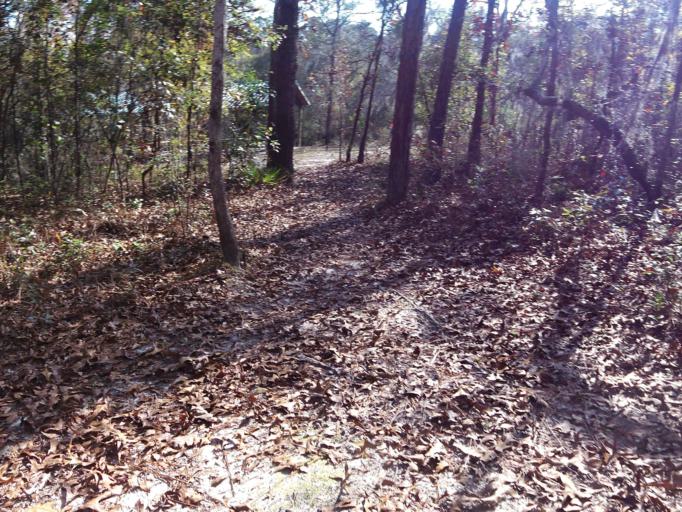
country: US
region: Florida
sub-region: Clay County
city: Middleburg
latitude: 30.1562
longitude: -81.9728
